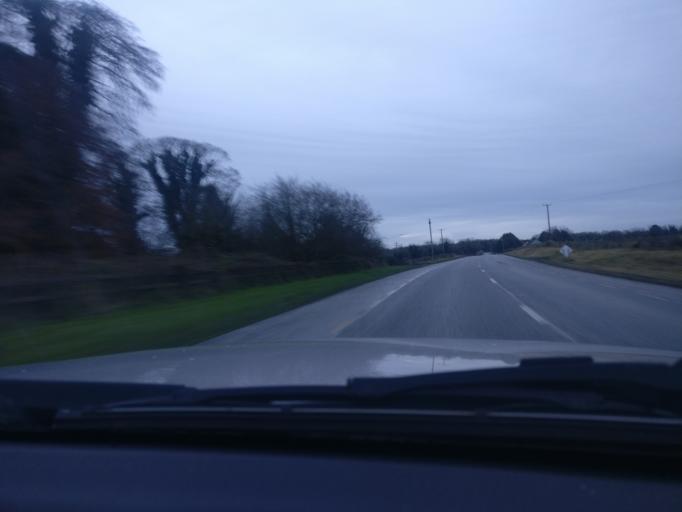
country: IE
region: Leinster
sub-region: An Mhi
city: Navan
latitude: 53.6659
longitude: -6.7276
